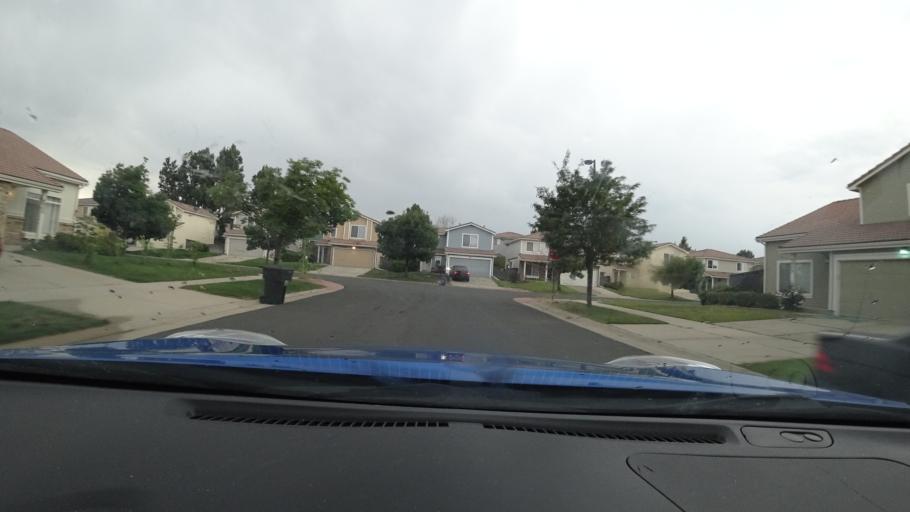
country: US
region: Colorado
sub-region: Adams County
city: Aurora
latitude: 39.7722
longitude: -104.7400
